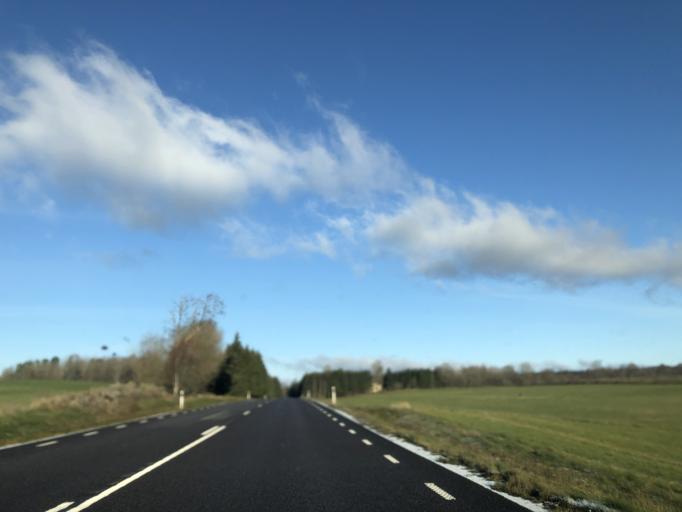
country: SE
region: Vaestra Goetaland
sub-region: Tranemo Kommun
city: Limmared
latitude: 57.6376
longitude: 13.4452
